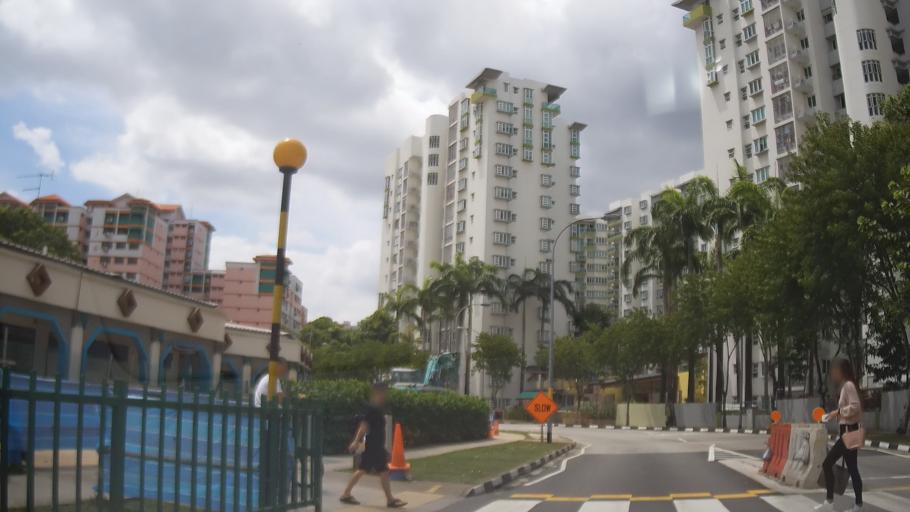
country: MY
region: Johor
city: Johor Bahru
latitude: 1.3862
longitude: 103.7440
